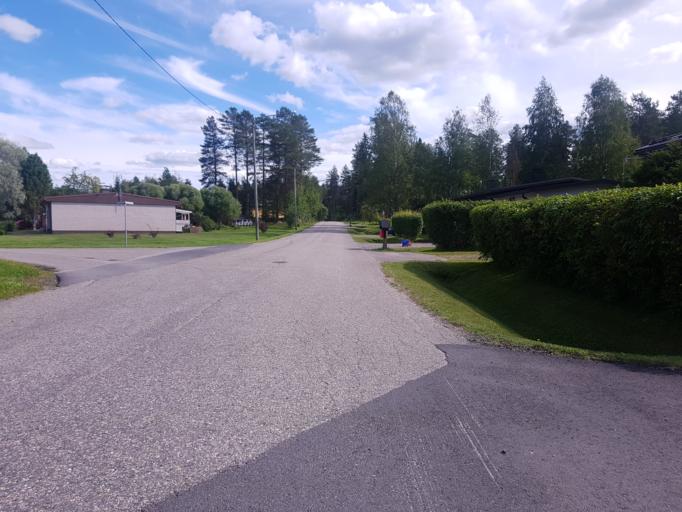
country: FI
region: Kainuu
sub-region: Kehys-Kainuu
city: Kuhmo
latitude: 64.1234
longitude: 29.5373
